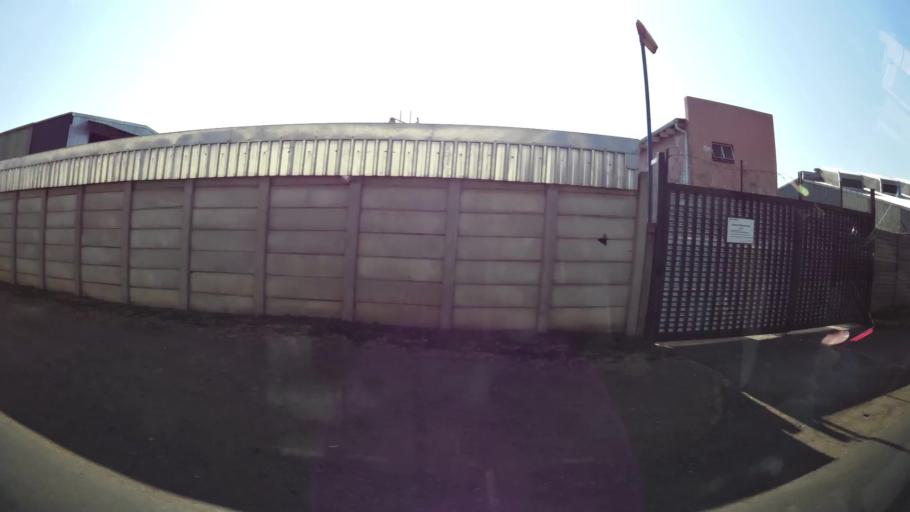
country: ZA
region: Gauteng
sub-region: City of Johannesburg Metropolitan Municipality
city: Modderfontein
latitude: -26.1432
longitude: 28.2081
